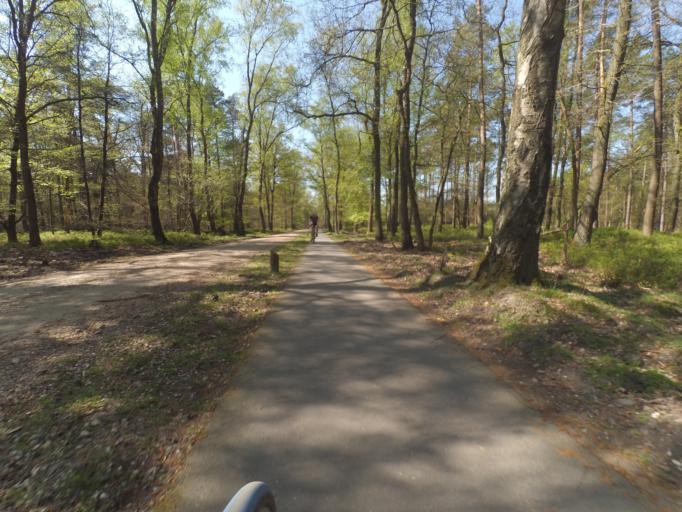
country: NL
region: Gelderland
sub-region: Gemeente Apeldoorn
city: Apeldoorn
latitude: 52.1980
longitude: 5.8857
